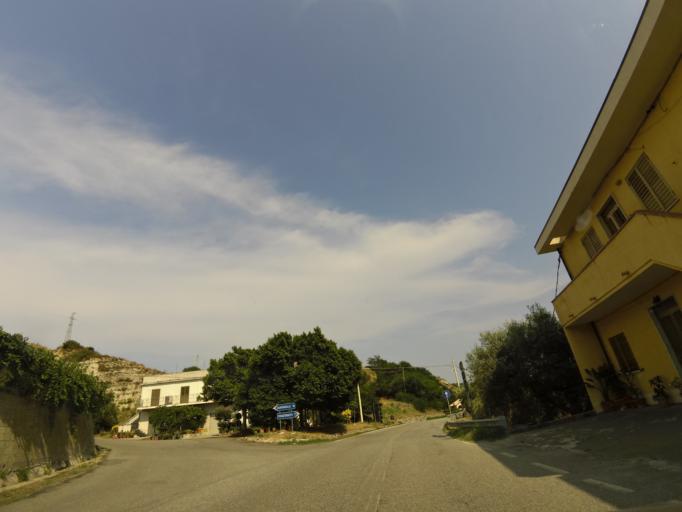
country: IT
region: Calabria
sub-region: Provincia di Catanzaro
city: Guardavalle
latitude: 38.4649
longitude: 16.5113
